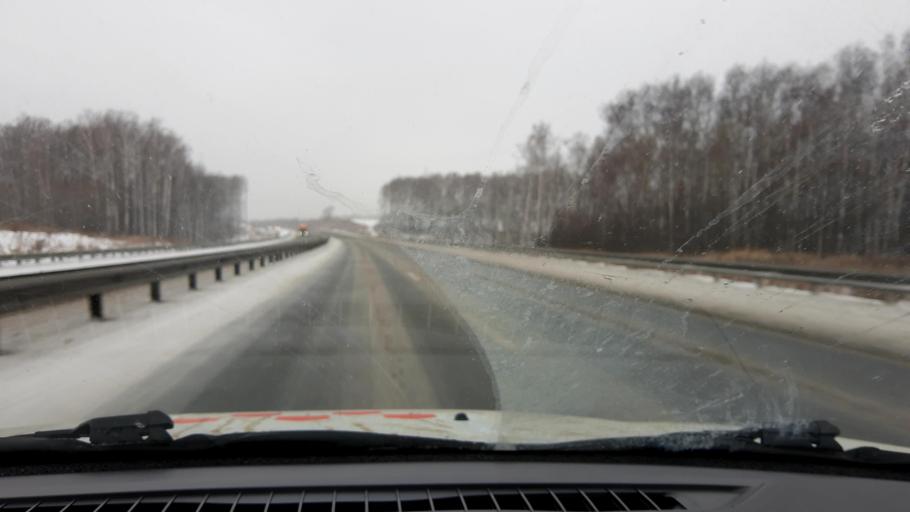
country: RU
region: Nizjnij Novgorod
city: Kstovo
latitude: 56.0985
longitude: 44.0611
